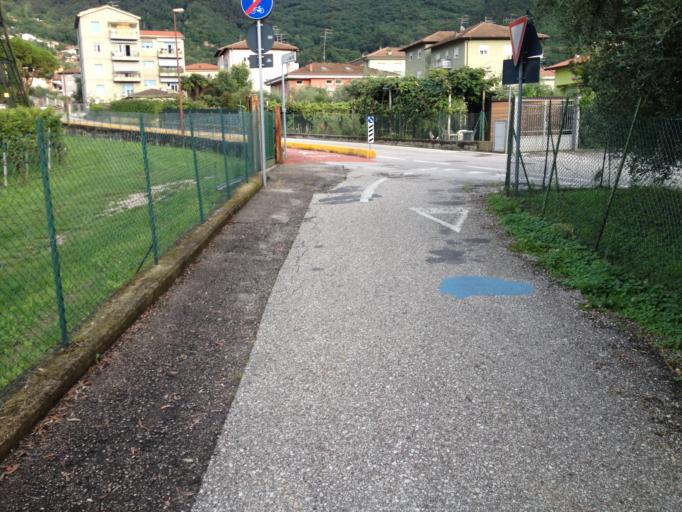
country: IT
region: Trentino-Alto Adige
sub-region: Provincia di Trento
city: Bolognano-Vignole
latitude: 45.9135
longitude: 10.9001
